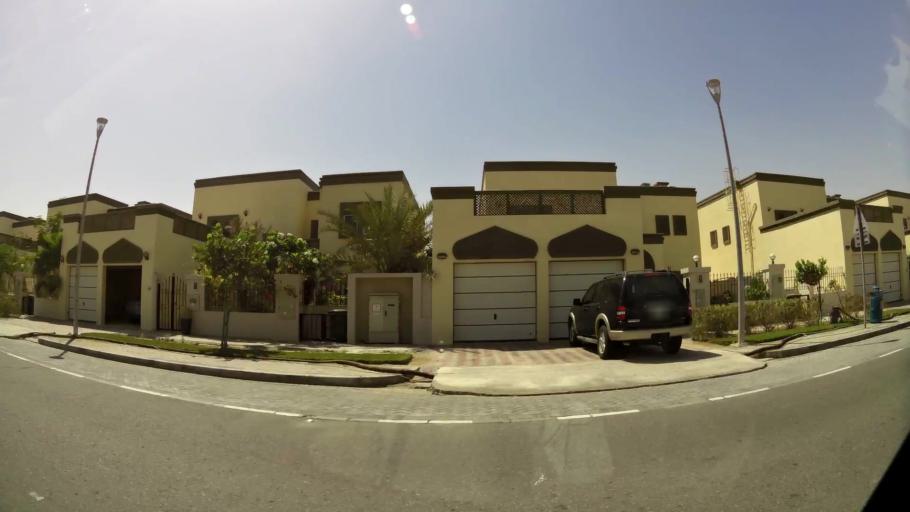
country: AE
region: Dubai
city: Dubai
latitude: 25.0435
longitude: 55.1545
